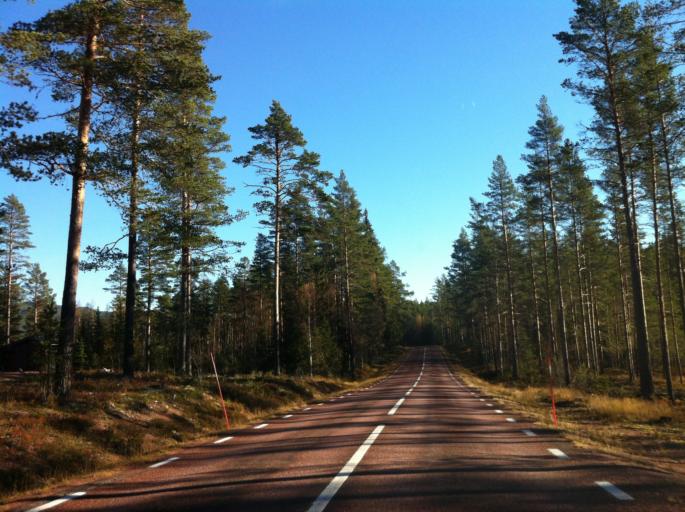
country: SE
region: Dalarna
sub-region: Alvdalens Kommun
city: AElvdalen
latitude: 61.3157
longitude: 13.6612
